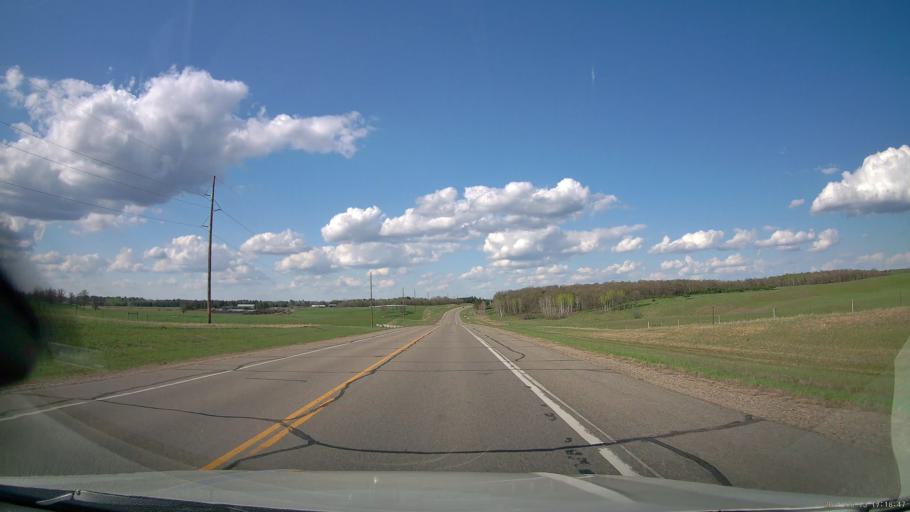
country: US
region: Minnesota
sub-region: Hubbard County
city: Park Rapids
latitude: 46.9670
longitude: -95.0162
